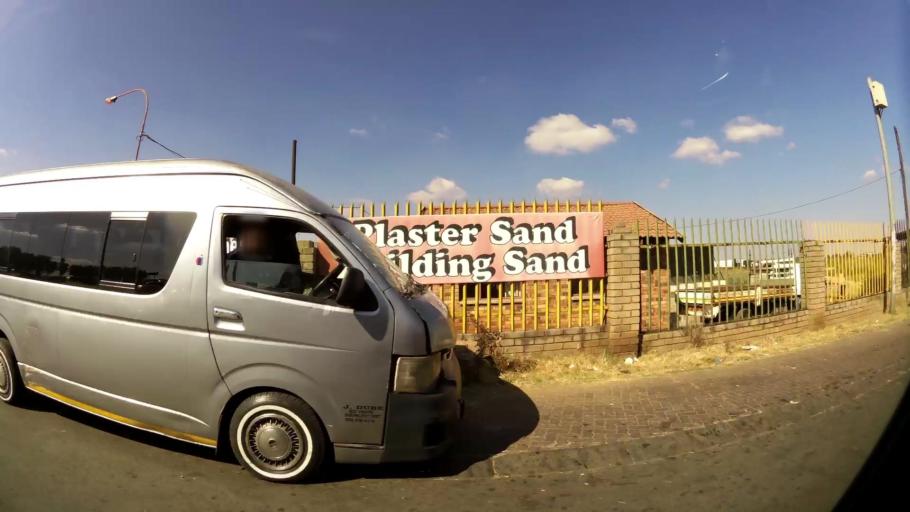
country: ZA
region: Gauteng
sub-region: City of Johannesburg Metropolitan Municipality
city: Soweto
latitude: -26.2399
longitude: 27.9118
